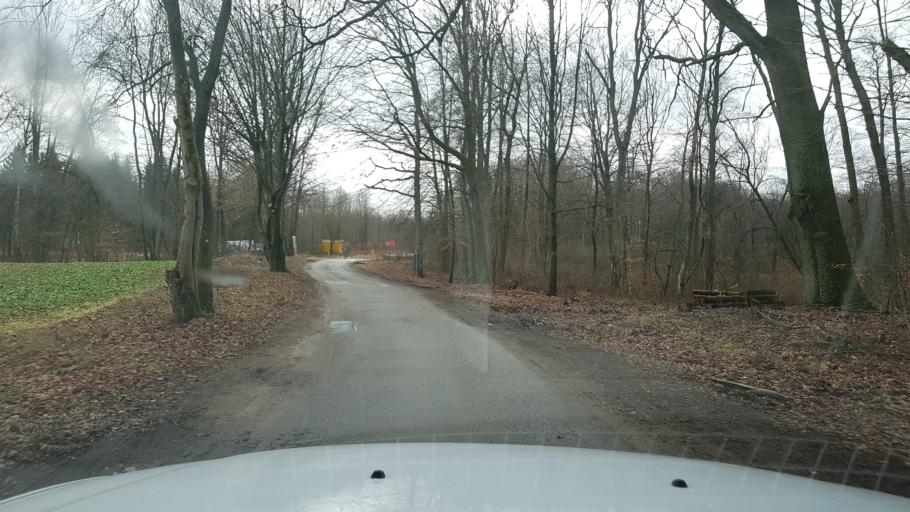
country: PL
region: West Pomeranian Voivodeship
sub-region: Powiat szczecinecki
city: Szczecinek
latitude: 53.7010
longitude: 16.7666
